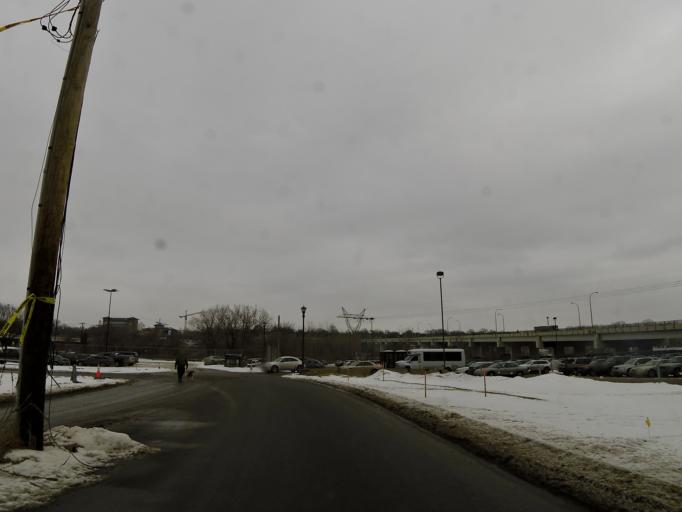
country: US
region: Minnesota
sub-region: Ramsey County
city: Saint Paul
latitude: 44.9512
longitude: -93.0801
